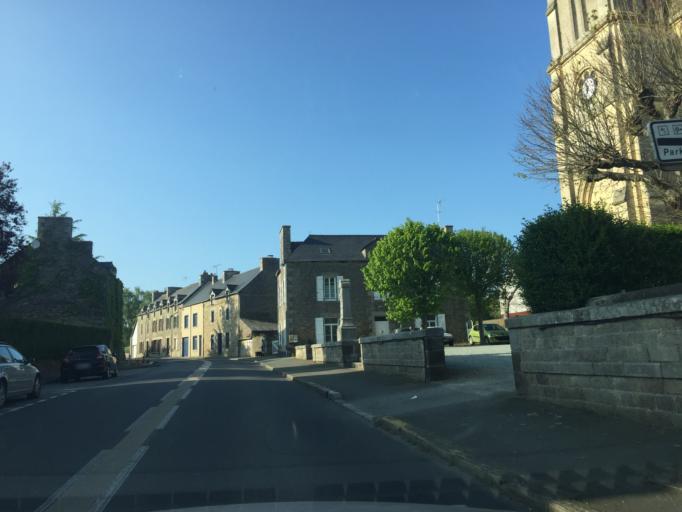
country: FR
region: Brittany
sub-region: Departement des Cotes-d'Armor
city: Crehen
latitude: 48.5454
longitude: -2.2296
